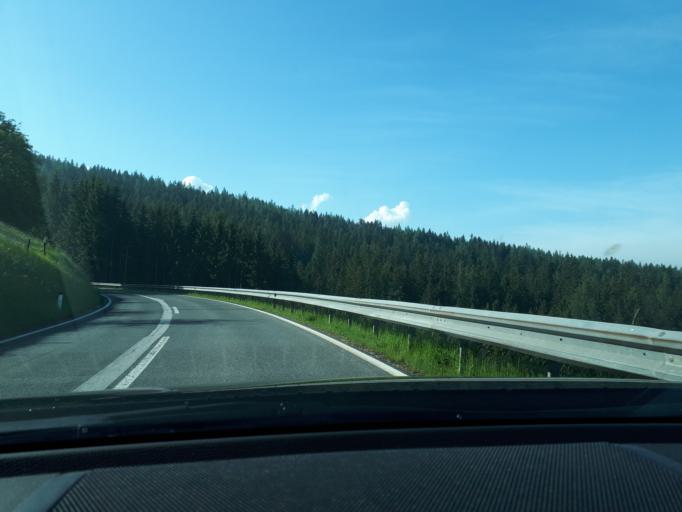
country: AT
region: Styria
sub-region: Politischer Bezirk Voitsberg
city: Pack
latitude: 46.9469
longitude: 14.9674
